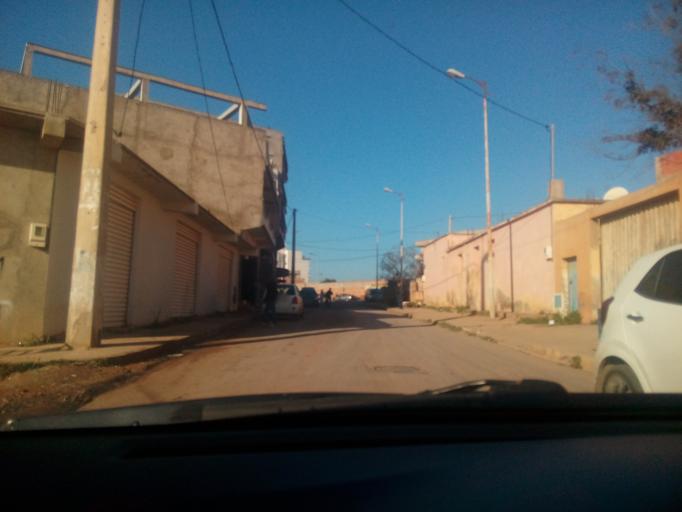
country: DZ
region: Oran
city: Bir el Djir
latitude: 35.7567
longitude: -0.5378
